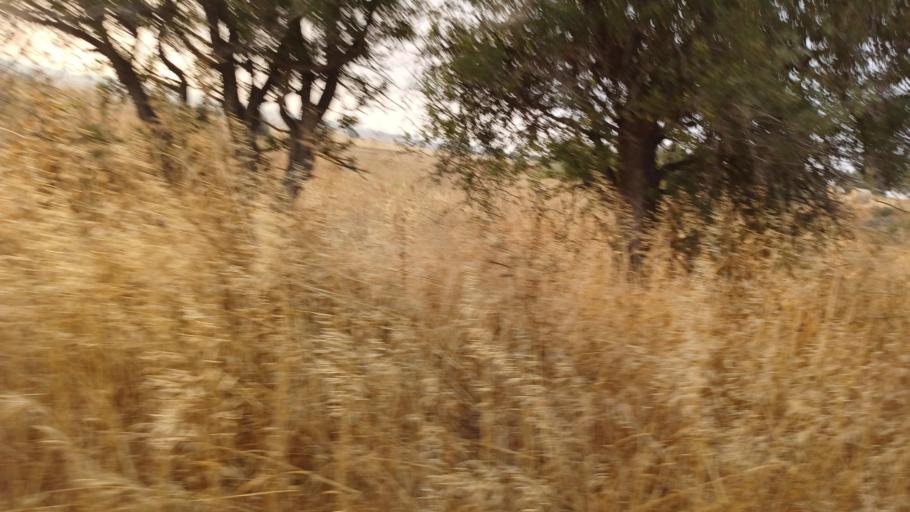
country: CY
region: Larnaka
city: Tersefanou
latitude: 34.8291
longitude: 33.5212
